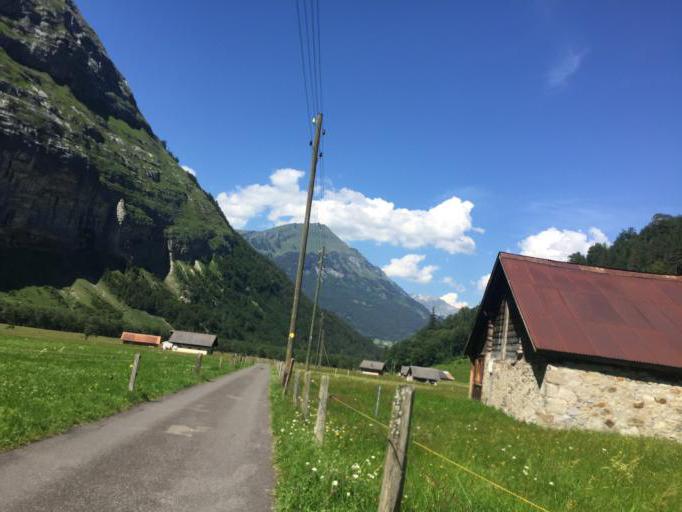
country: CH
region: Bern
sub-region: Interlaken-Oberhasli District
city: Meiringen
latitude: 46.6815
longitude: 8.2115
